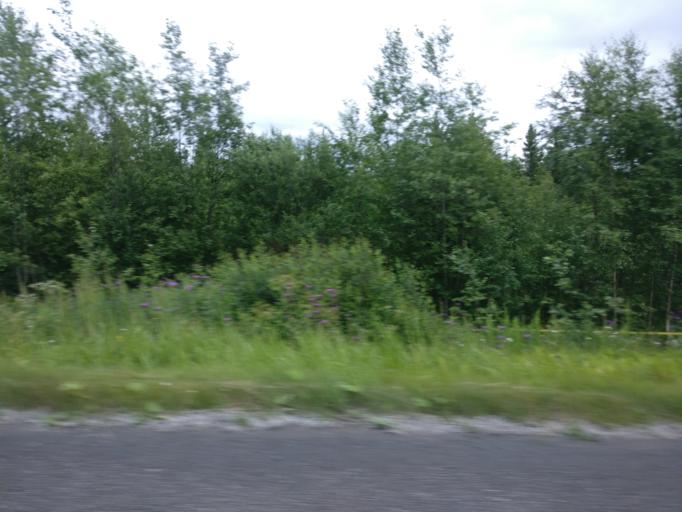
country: FI
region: Northern Savo
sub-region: Varkaus
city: Varkaus
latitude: 62.3864
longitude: 27.8102
